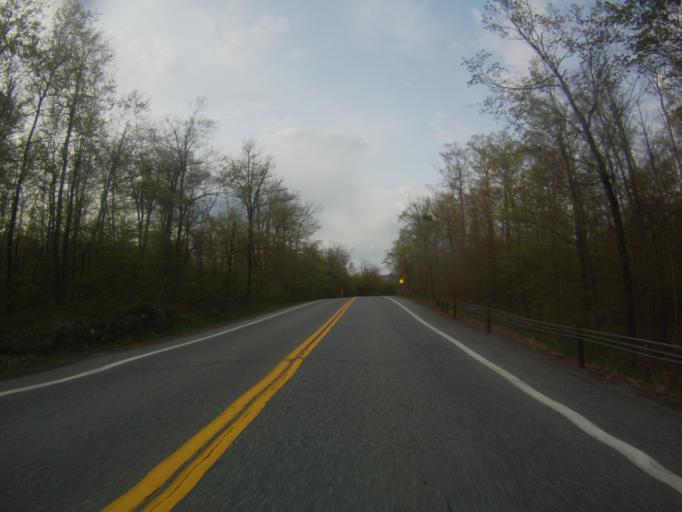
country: US
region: New York
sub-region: Essex County
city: Ticonderoga
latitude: 43.7490
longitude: -73.5717
